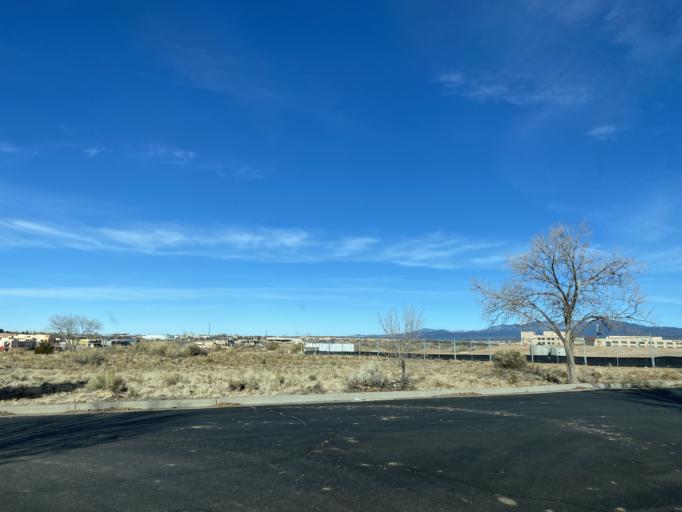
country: US
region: New Mexico
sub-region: Santa Fe County
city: Agua Fria
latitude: 35.6117
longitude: -106.0312
